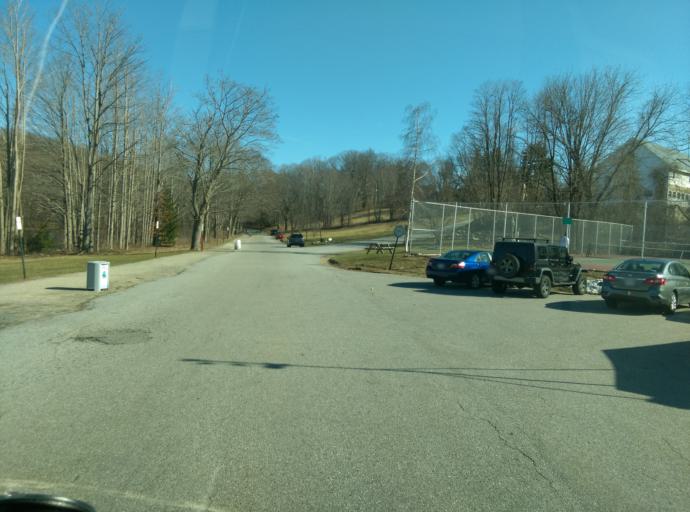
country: US
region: Massachusetts
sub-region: Essex County
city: Haverhill
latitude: 42.7906
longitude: -71.0687
